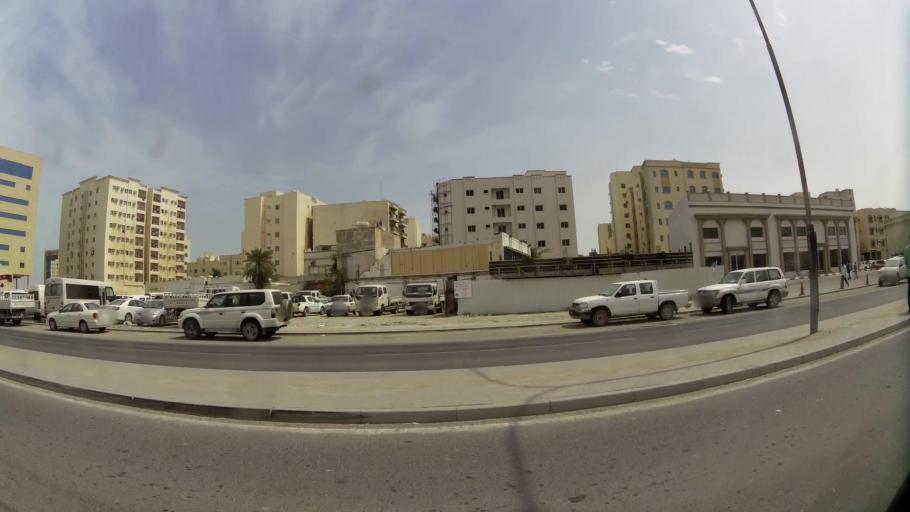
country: QA
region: Baladiyat ad Dawhah
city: Doha
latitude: 25.2813
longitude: 51.5368
